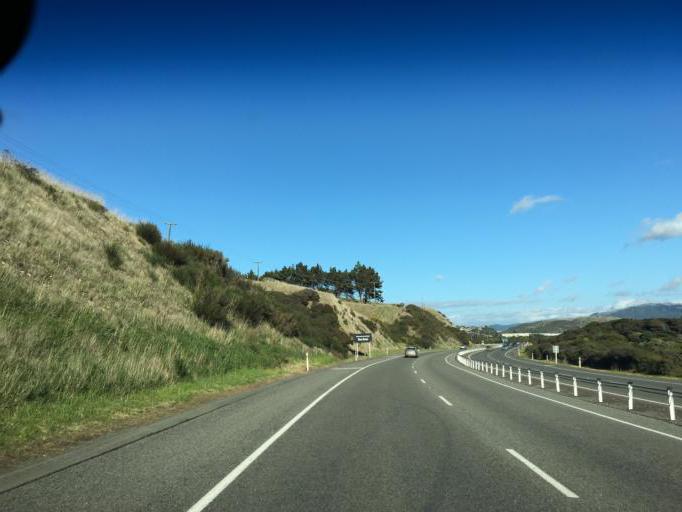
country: NZ
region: Wellington
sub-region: Porirua City
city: Porirua
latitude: -41.0685
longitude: 174.8772
